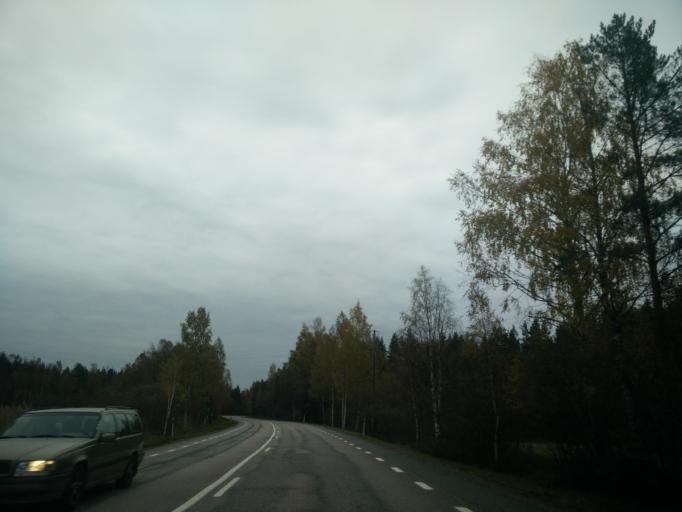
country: SE
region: Gaevleborg
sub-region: Gavle Kommun
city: Norrsundet
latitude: 60.8827
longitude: 17.1378
